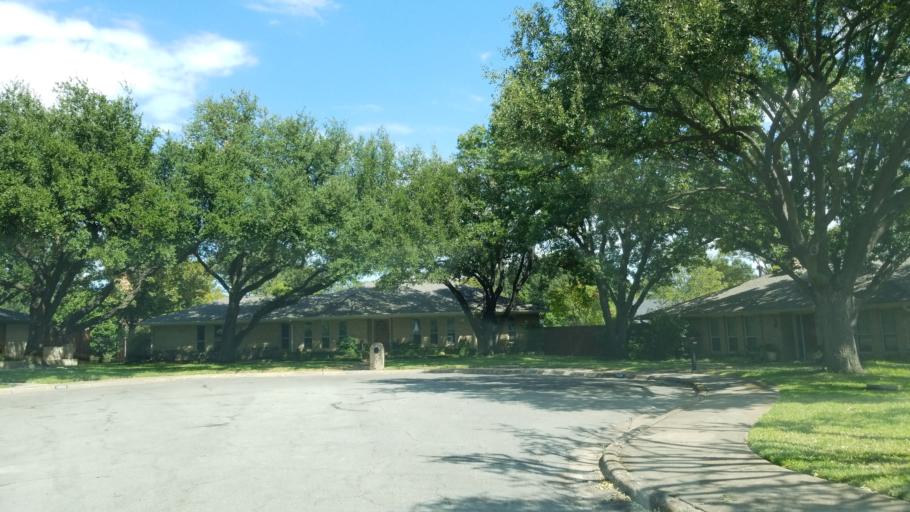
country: US
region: Texas
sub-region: Dallas County
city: Addison
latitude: 32.9535
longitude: -96.7838
